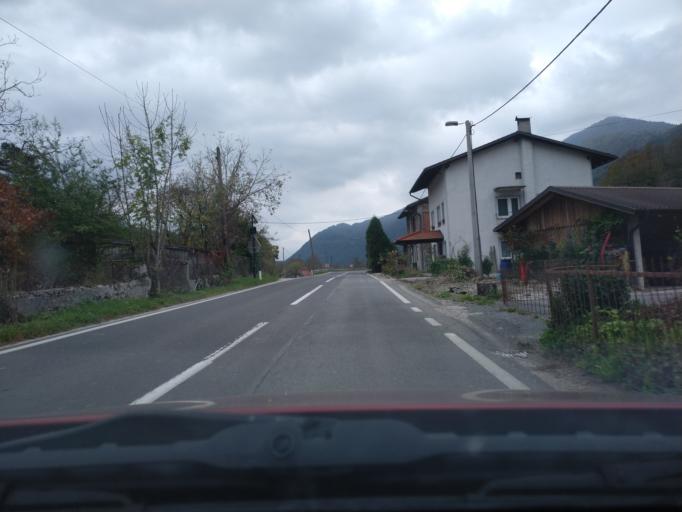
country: SI
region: Kobarid
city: Kobarid
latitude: 46.2312
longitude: 13.5940
